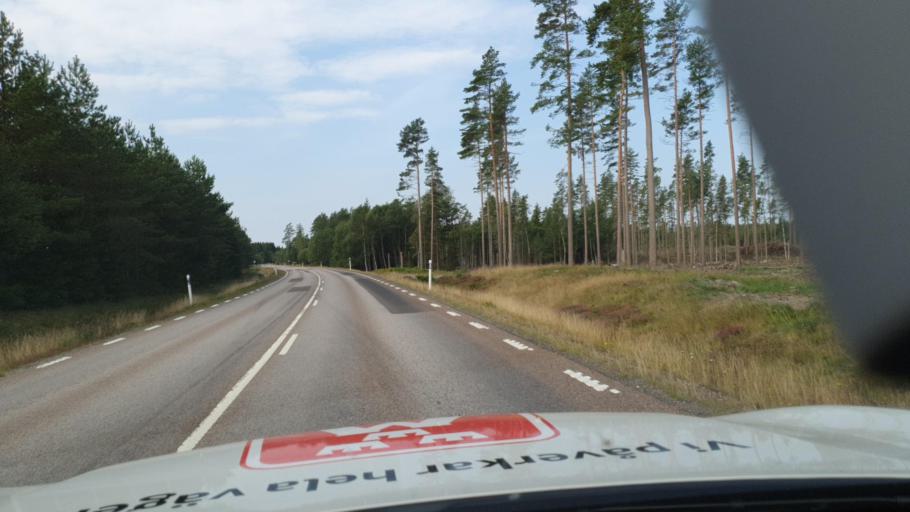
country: SE
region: Vaestra Goetaland
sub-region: Melleruds Kommun
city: Mellerud
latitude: 58.7504
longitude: 12.3196
